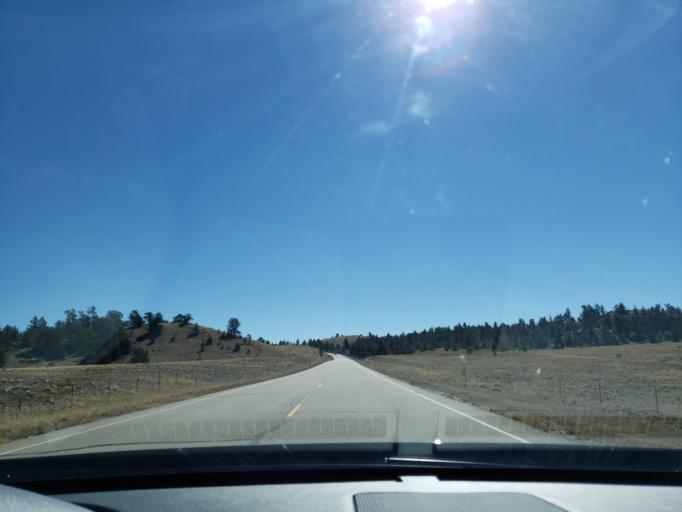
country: US
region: Colorado
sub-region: Chaffee County
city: Buena Vista
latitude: 38.8981
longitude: -105.6926
